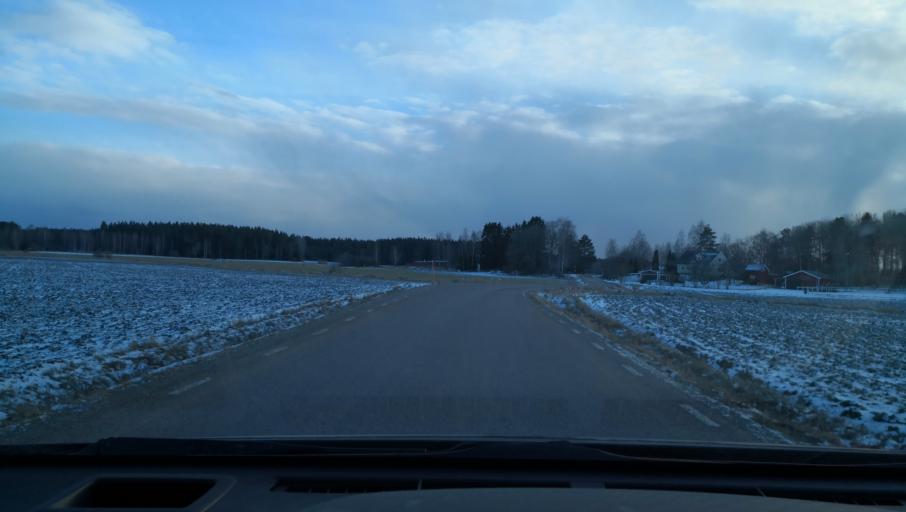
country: SE
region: Vaestmanland
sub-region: Vasteras
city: Tillberga
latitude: 59.6444
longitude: 16.7438
